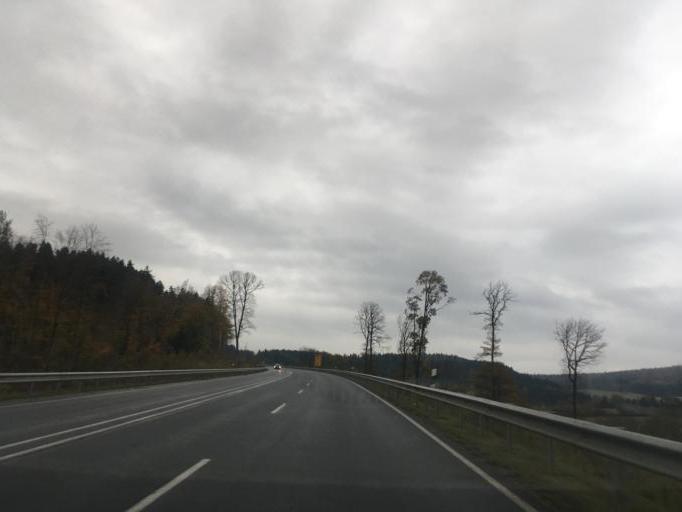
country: DE
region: Lower Saxony
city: Hardegsen
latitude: 51.6524
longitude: 9.7643
